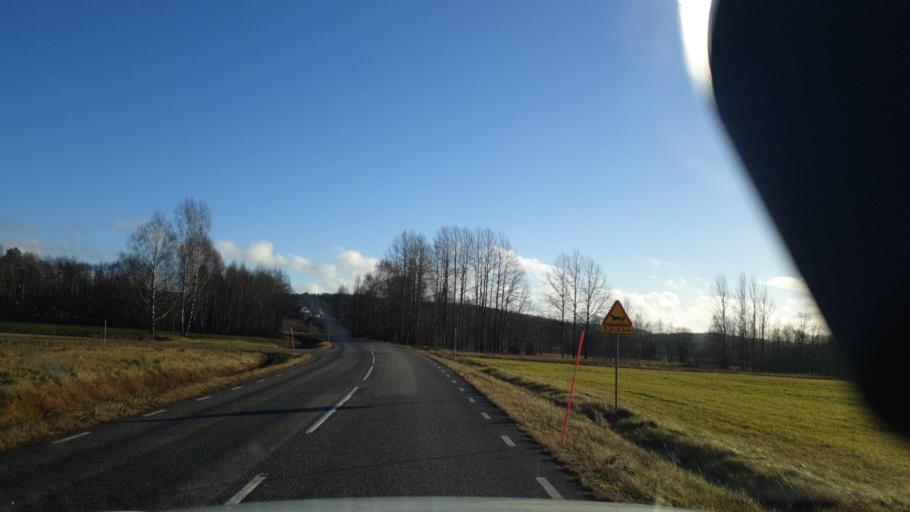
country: SE
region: Vaermland
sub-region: Eda Kommun
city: Amotfors
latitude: 59.6856
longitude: 12.1000
